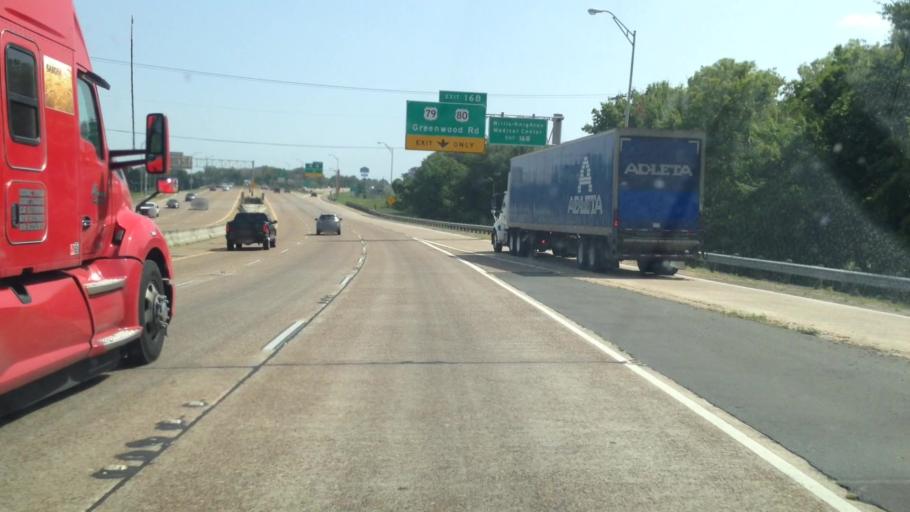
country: US
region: Louisiana
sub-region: Caddo Parish
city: Shreveport
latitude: 32.4900
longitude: -93.7725
